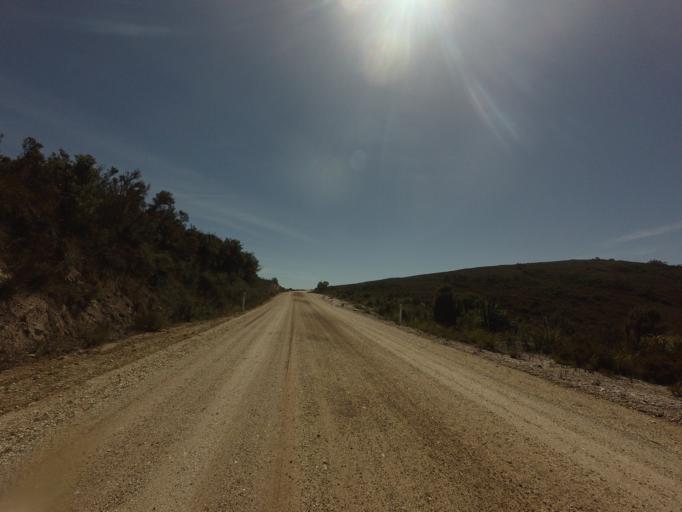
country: AU
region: Tasmania
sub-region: Huon Valley
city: Geeveston
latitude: -43.0348
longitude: 146.3335
